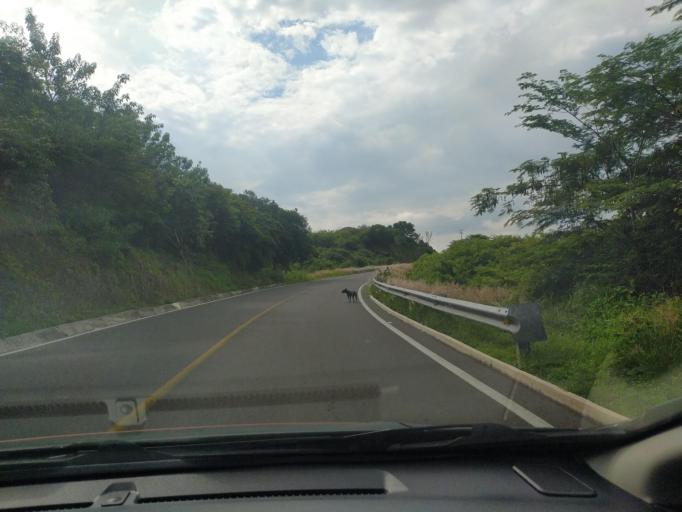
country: MX
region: Jalisco
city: Villa Corona
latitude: 20.3940
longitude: -103.6775
